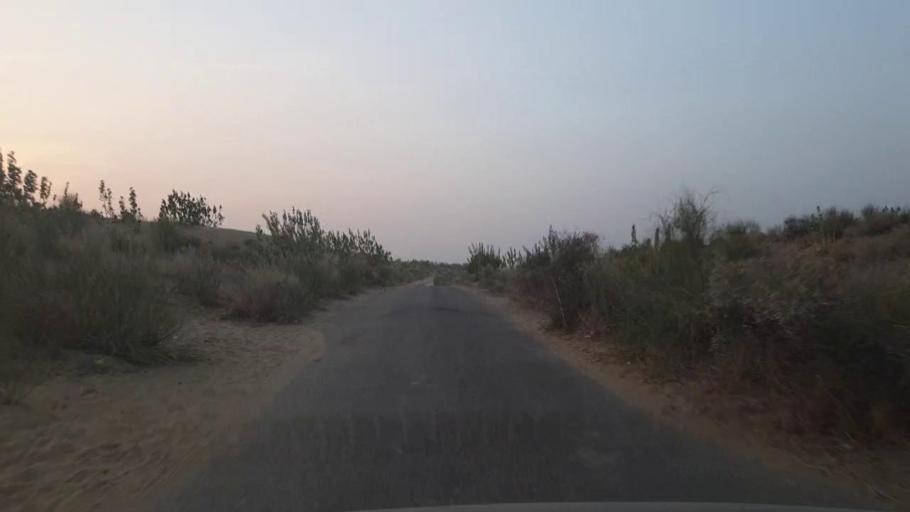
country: PK
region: Sindh
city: Umarkot
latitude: 25.3397
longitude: 70.0534
